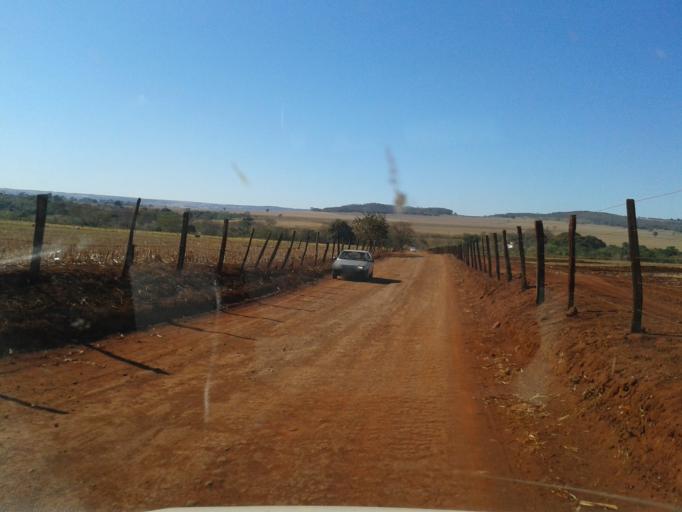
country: BR
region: Minas Gerais
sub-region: Centralina
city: Centralina
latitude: -18.5868
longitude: -49.1840
